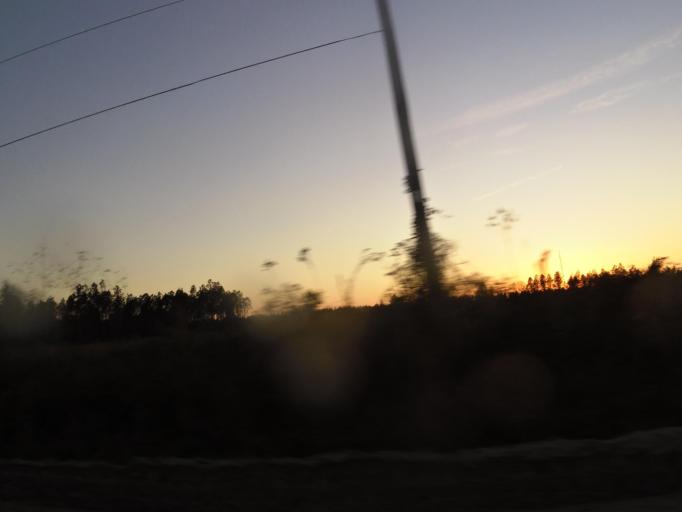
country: US
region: Florida
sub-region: Clay County
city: Asbury Lake
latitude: 29.9633
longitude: -81.7933
